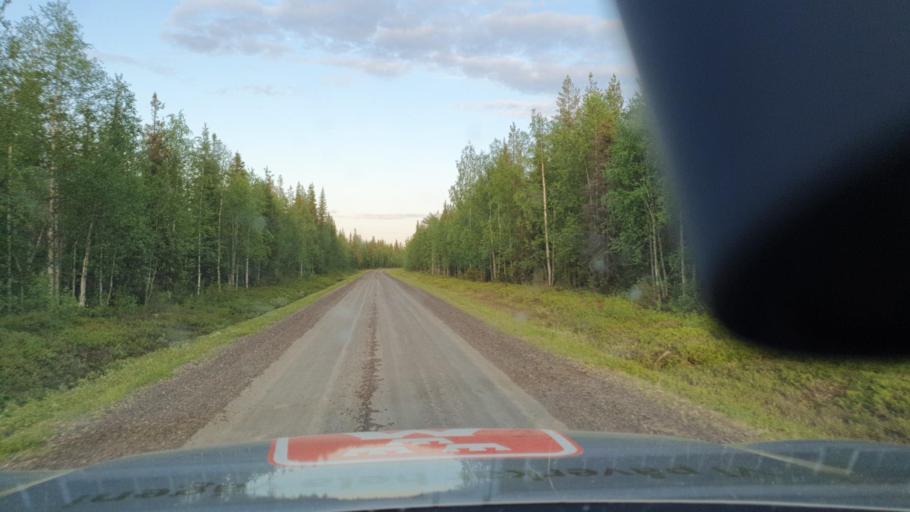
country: SE
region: Norrbotten
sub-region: Bodens Kommun
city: Boden
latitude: 66.4883
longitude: 21.5888
